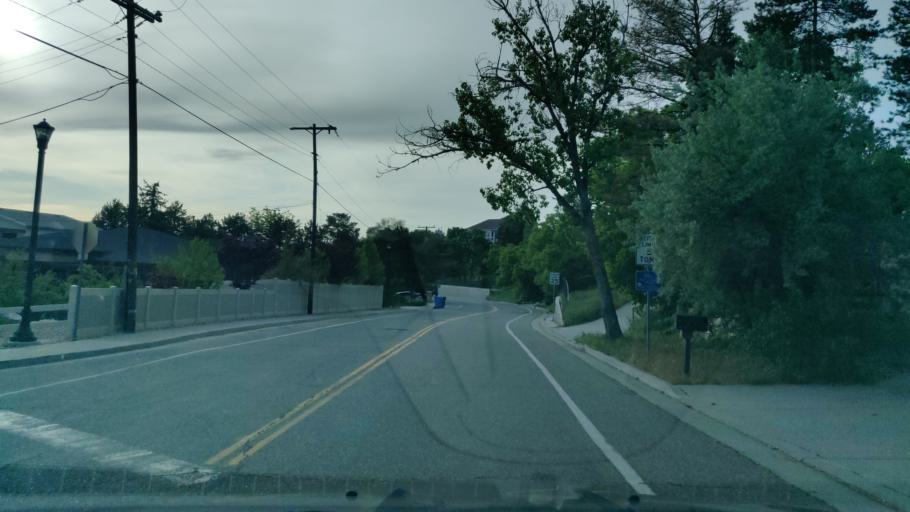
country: US
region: Utah
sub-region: Salt Lake County
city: Cottonwood Heights
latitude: 40.6047
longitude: -111.8054
